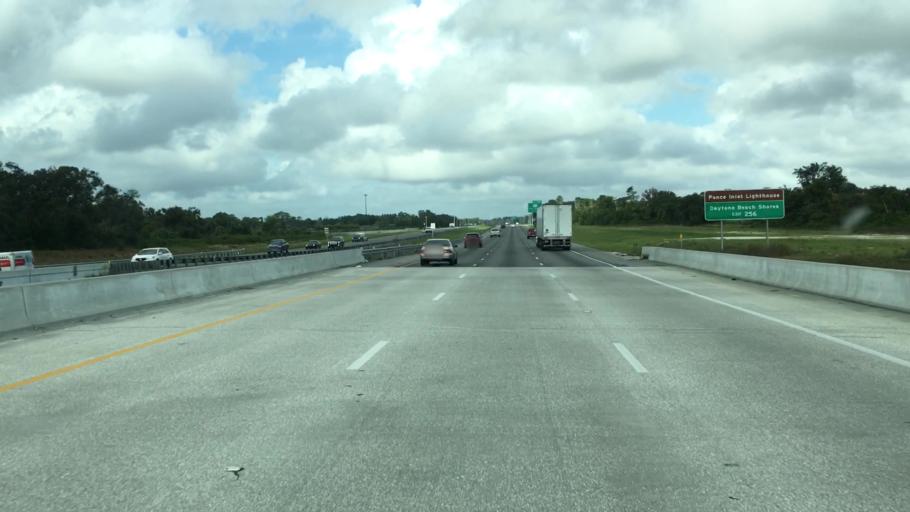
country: US
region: Florida
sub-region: Volusia County
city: Port Orange
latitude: 29.0921
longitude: -81.0216
